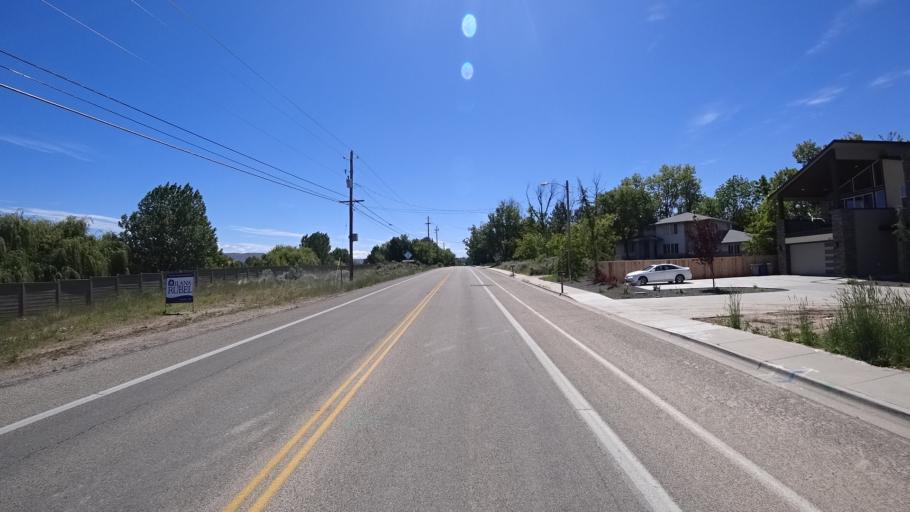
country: US
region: Idaho
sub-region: Ada County
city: Boise
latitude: 43.5721
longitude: -116.1540
